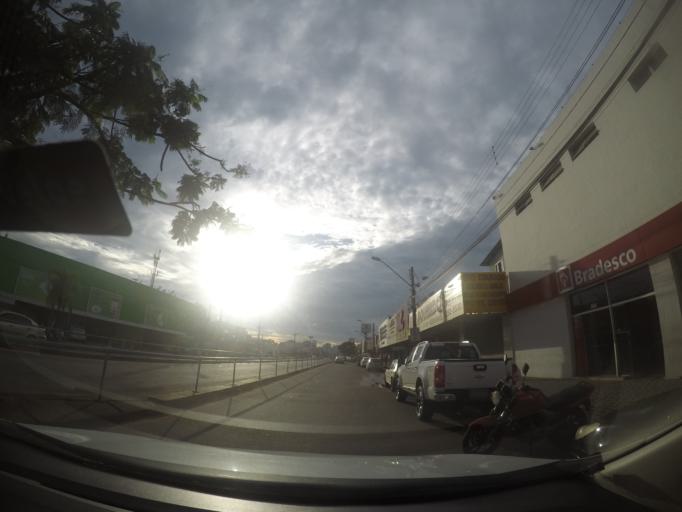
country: BR
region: Goias
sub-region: Goiania
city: Goiania
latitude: -16.6740
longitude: -49.2840
